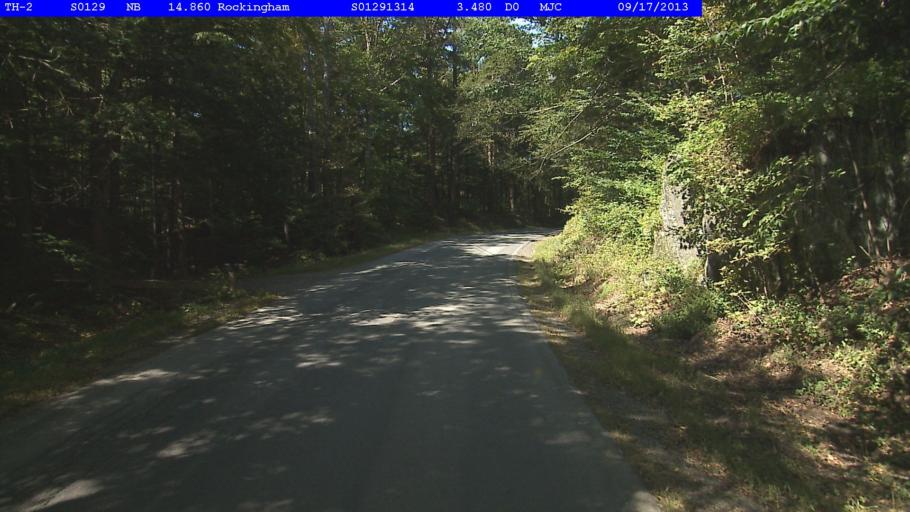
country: US
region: Vermont
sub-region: Windham County
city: Rockingham
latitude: 43.1674
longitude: -72.5174
